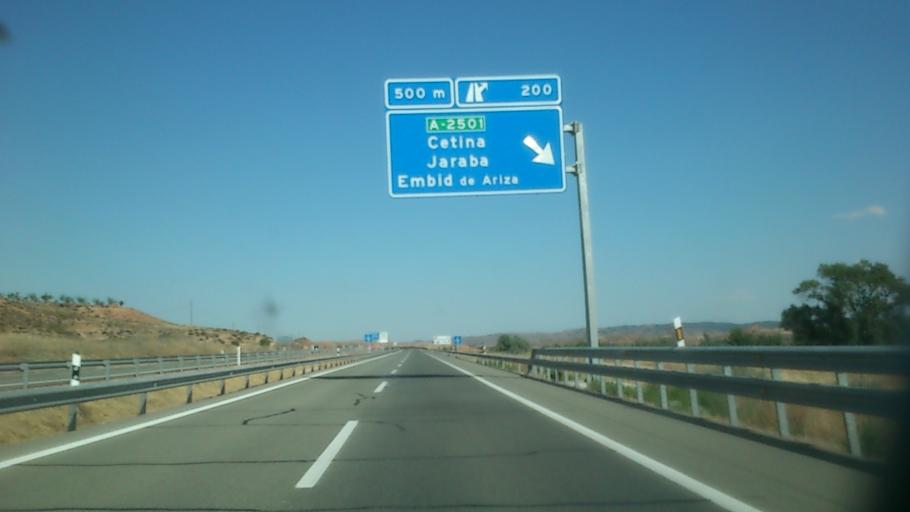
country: ES
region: Aragon
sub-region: Provincia de Zaragoza
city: Cetina
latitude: 41.3055
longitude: -1.9791
